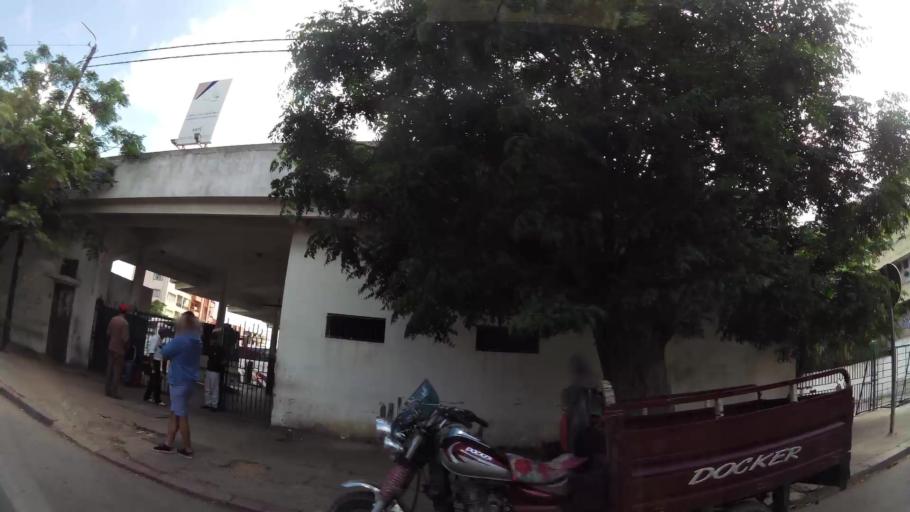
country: MA
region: Gharb-Chrarda-Beni Hssen
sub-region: Kenitra Province
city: Kenitra
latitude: 34.2647
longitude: -6.5746
